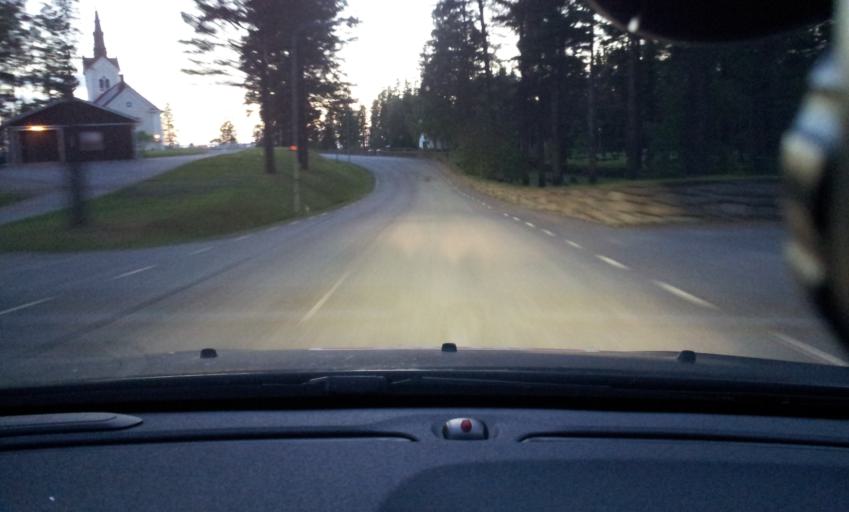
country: SE
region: Jaemtland
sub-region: Braecke Kommun
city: Braecke
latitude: 62.7421
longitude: 15.4326
